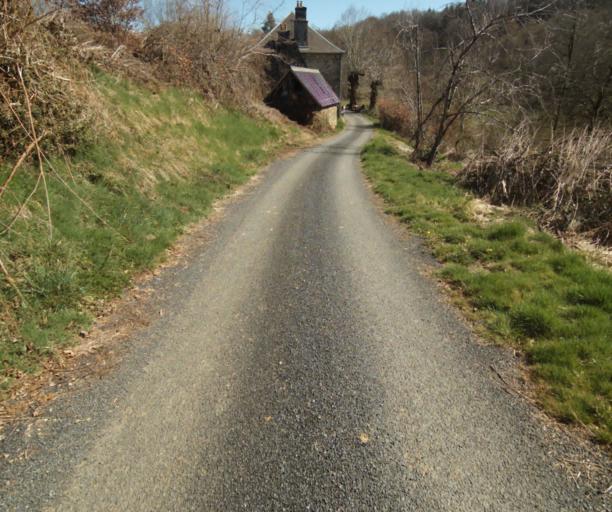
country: FR
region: Limousin
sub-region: Departement de la Correze
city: Chamboulive
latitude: 45.4388
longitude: 1.7301
